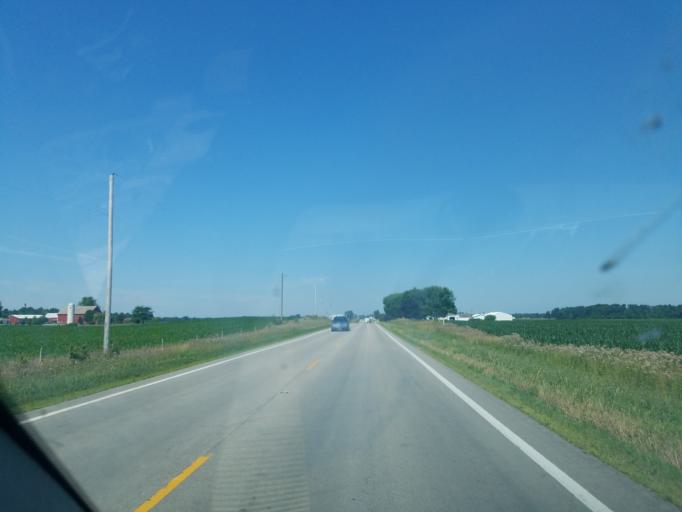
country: US
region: Ohio
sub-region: Shelby County
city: Botkins
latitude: 40.4389
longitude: -84.2373
